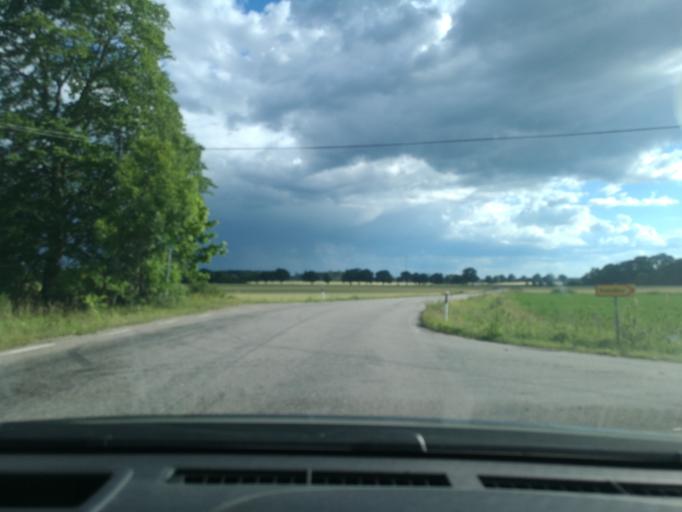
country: SE
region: Soedermanland
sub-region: Eskilstuna Kommun
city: Arla
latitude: 59.4478
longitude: 16.7234
